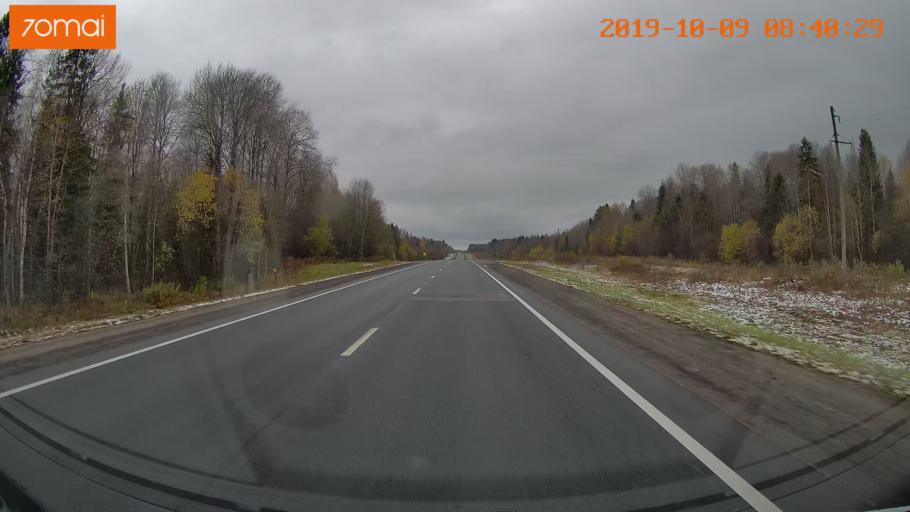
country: RU
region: Vologda
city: Gryazovets
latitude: 58.9872
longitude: 40.1398
